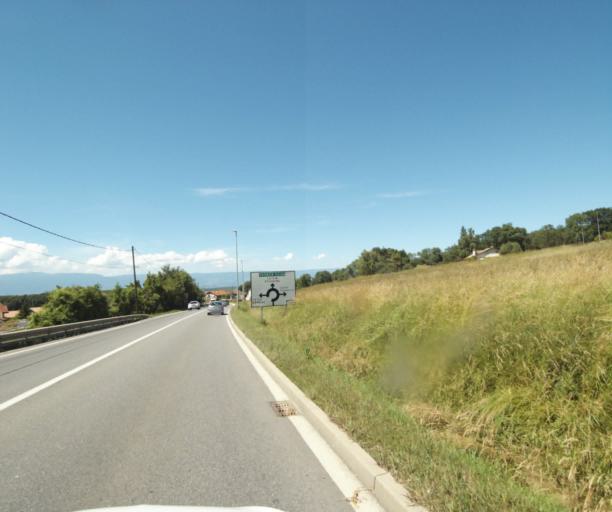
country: FR
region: Rhone-Alpes
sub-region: Departement de la Haute-Savoie
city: Loisin
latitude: 46.2689
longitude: 6.3142
